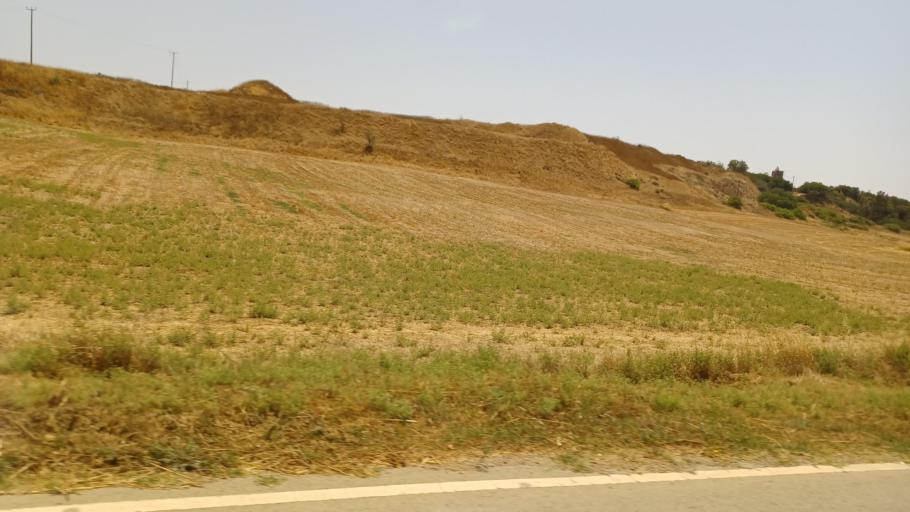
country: CY
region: Ammochostos
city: Avgorou
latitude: 35.0549
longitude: 33.8375
